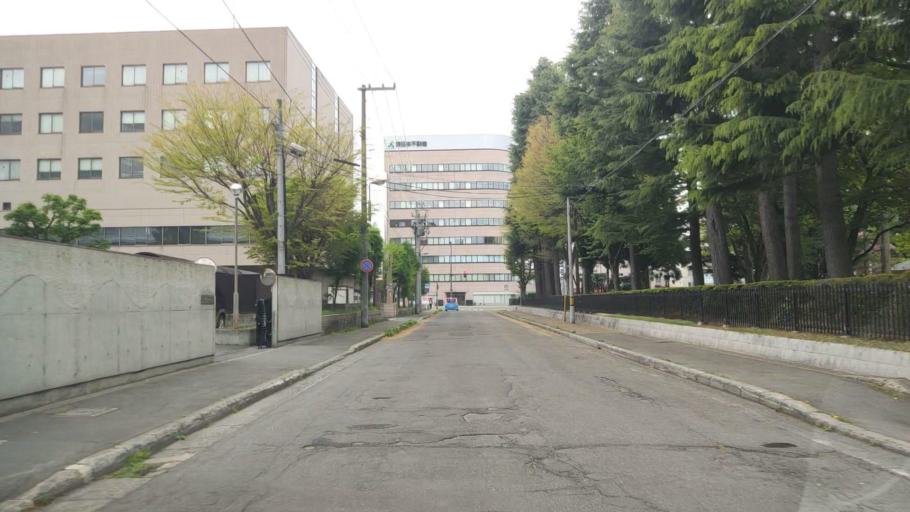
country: JP
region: Aomori
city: Aomori Shi
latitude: 40.8243
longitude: 140.7428
